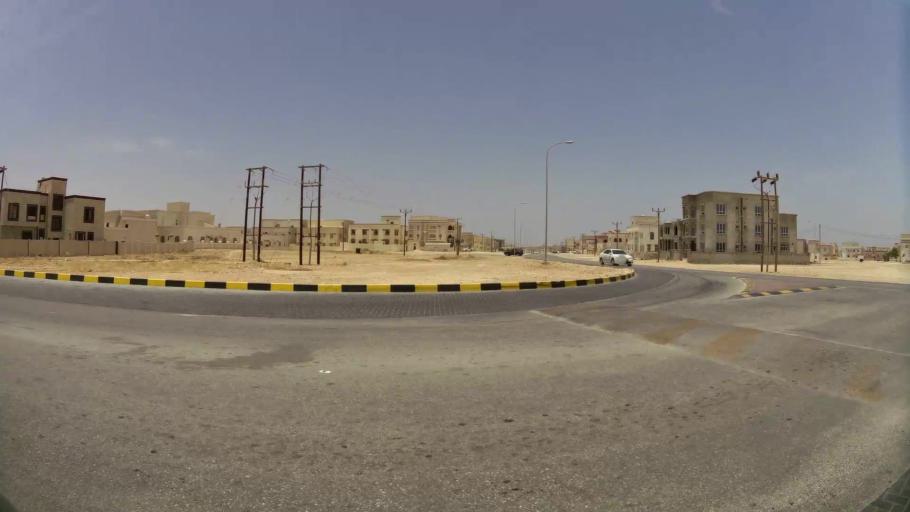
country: OM
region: Zufar
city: Salalah
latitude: 17.0816
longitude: 54.1586
